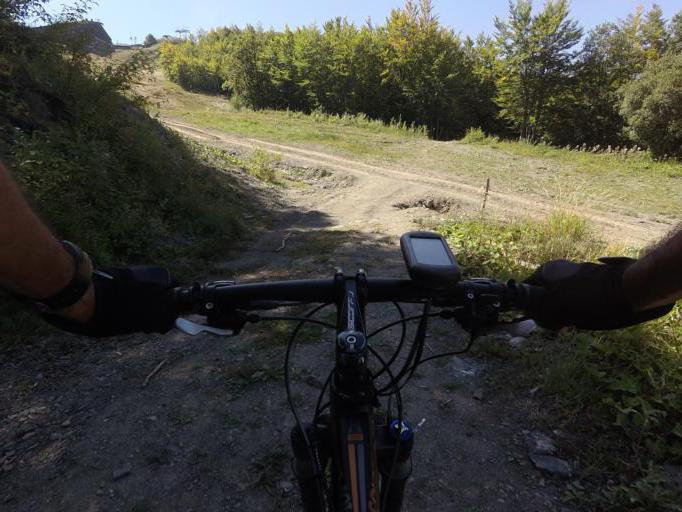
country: IT
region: Emilia-Romagna
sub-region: Provincia di Modena
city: Montecreto
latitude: 44.2176
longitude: 10.7201
